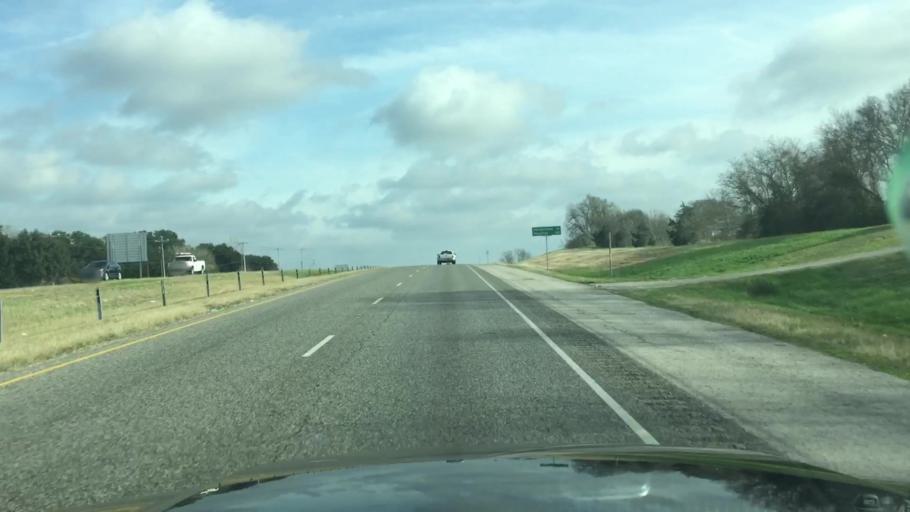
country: US
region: Texas
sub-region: Washington County
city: Brenham
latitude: 30.1397
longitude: -96.3556
